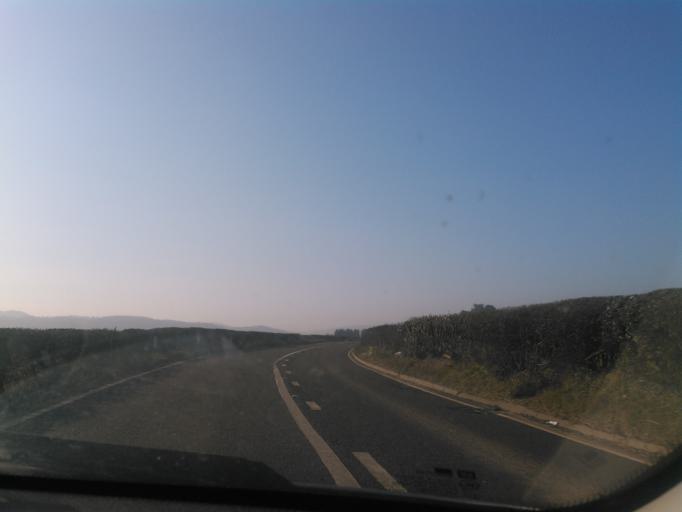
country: GB
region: England
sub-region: Shropshire
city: Craven Arms
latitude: 52.4860
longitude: -2.8160
